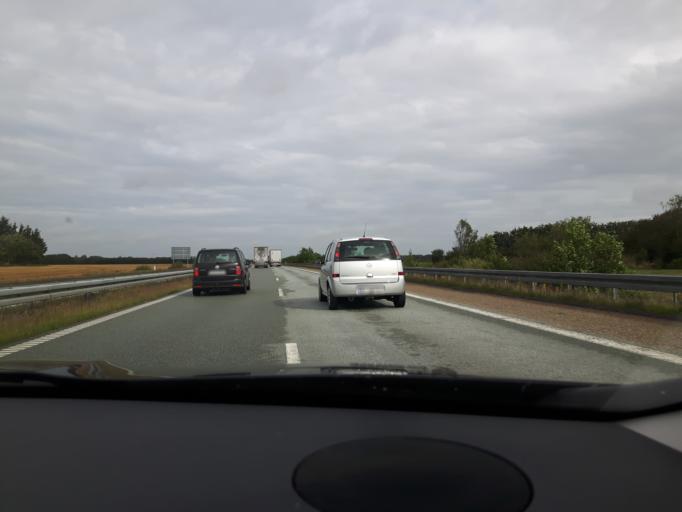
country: DK
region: North Denmark
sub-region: Hjorring Kommune
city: Hjorring
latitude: 57.4683
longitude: 10.0460
